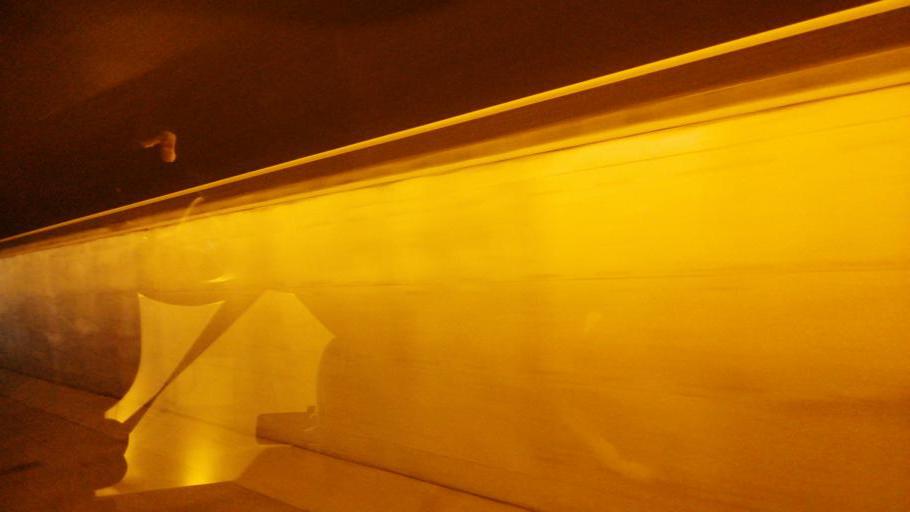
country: TR
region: Yalova
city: Altinova
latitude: 40.6971
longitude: 29.4854
